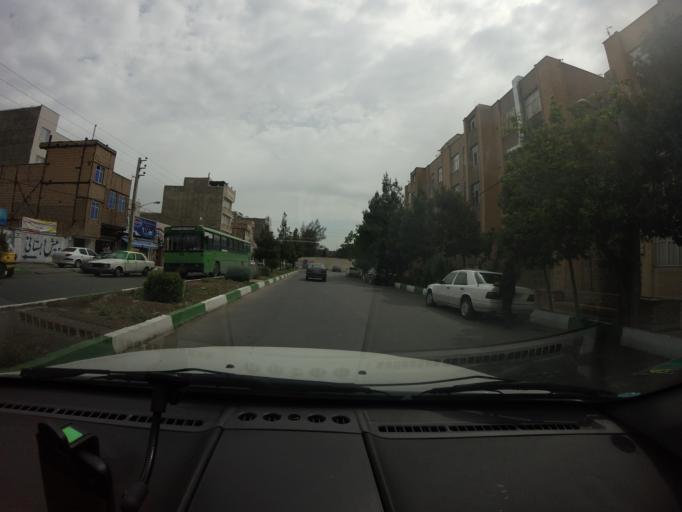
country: IR
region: Tehran
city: Eslamshahr
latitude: 35.5481
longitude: 51.2464
